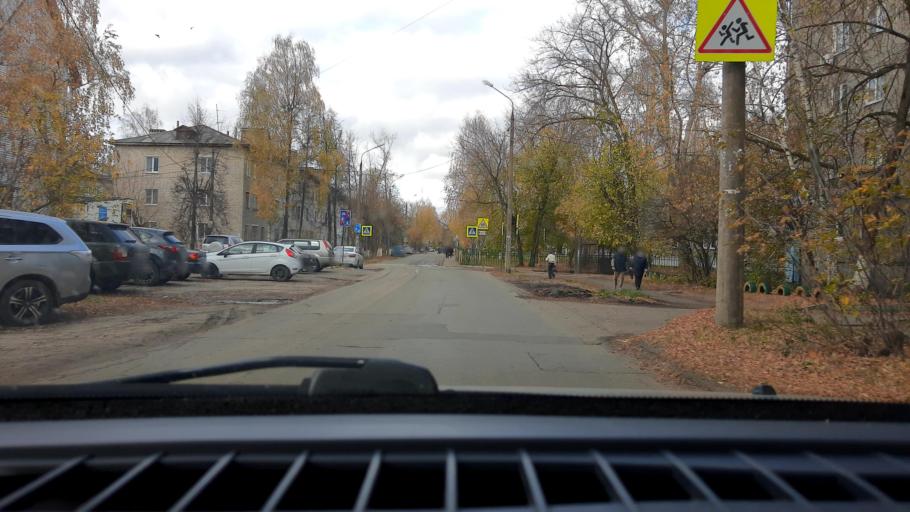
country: RU
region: Nizjnij Novgorod
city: Gorbatovka
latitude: 56.3527
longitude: 43.8374
